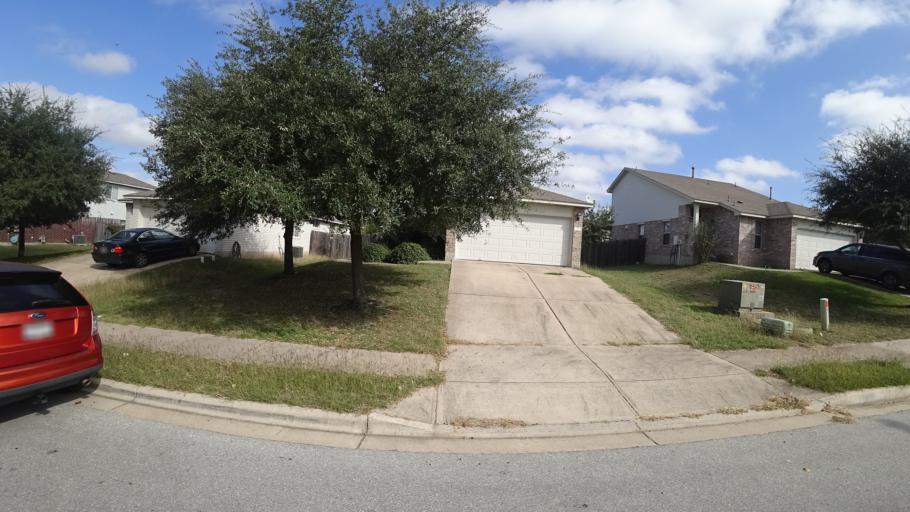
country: US
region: Texas
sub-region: Travis County
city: Pflugerville
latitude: 30.4258
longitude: -97.6424
